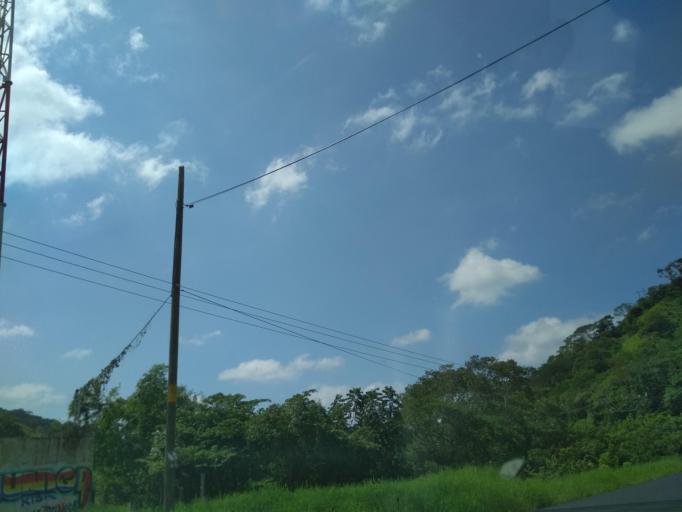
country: MX
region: Veracruz
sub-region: San Andres Tuxtla
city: Texcaltitan Xoteapan (Texcaltitan)
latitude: 18.4436
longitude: -95.2512
